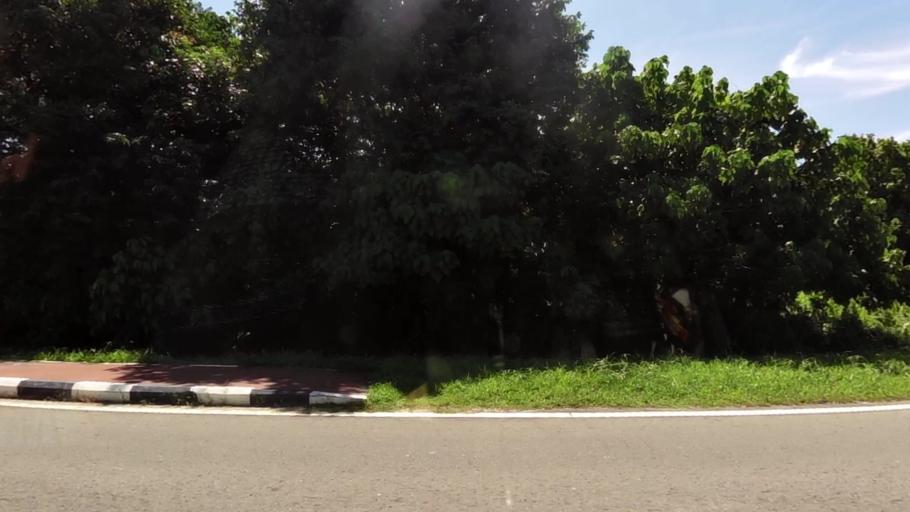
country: BN
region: Brunei and Muara
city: Bandar Seri Begawan
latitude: 4.9387
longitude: 114.9442
